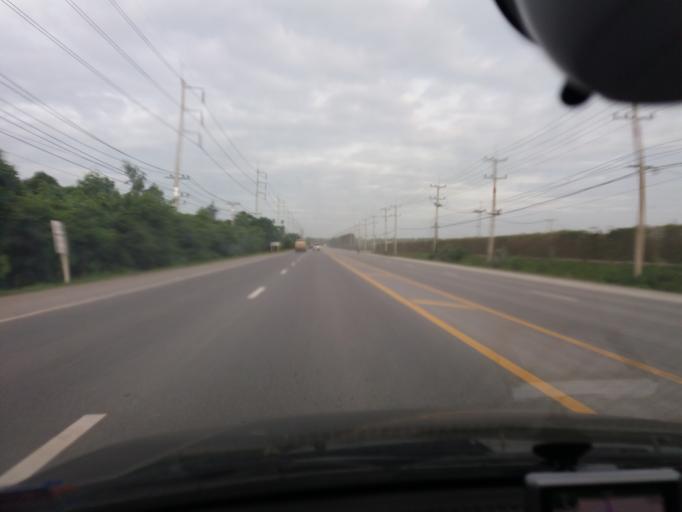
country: TH
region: Suphan Buri
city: U Thong
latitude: 14.3420
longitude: 99.8545
